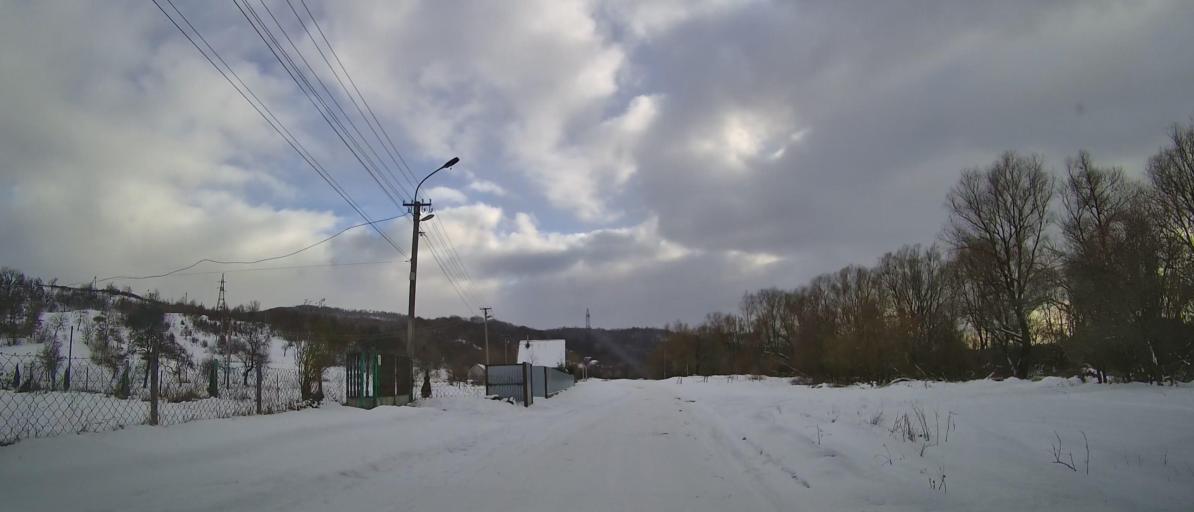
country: UA
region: Zakarpattia
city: Velykyi Bereznyi
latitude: 48.9102
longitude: 22.4664
